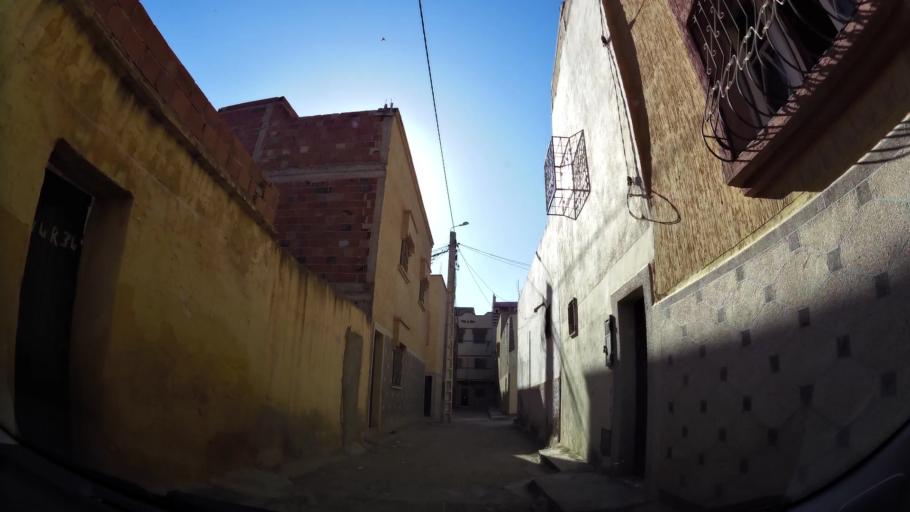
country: MA
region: Oriental
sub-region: Oujda-Angad
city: Oujda
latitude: 34.6603
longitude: -1.9053
